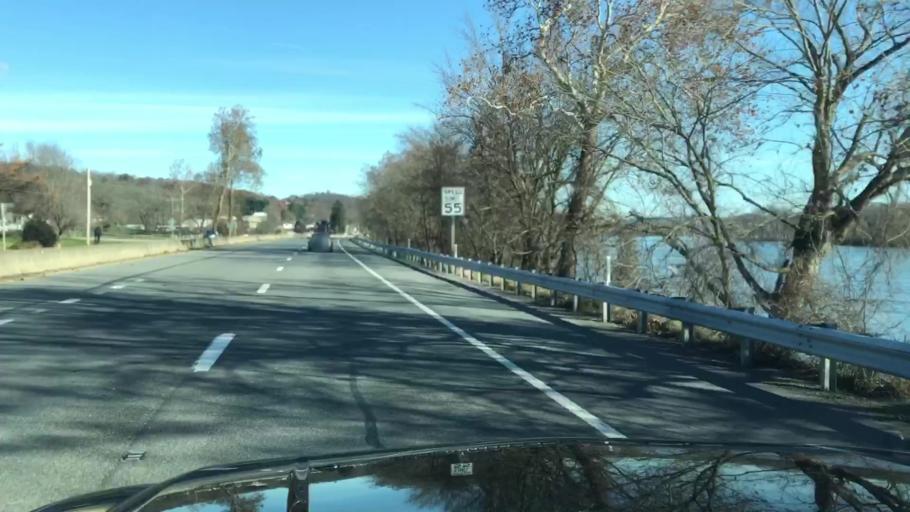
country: US
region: Pennsylvania
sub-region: Dauphin County
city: Millersburg
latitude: 40.6646
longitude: -76.9153
